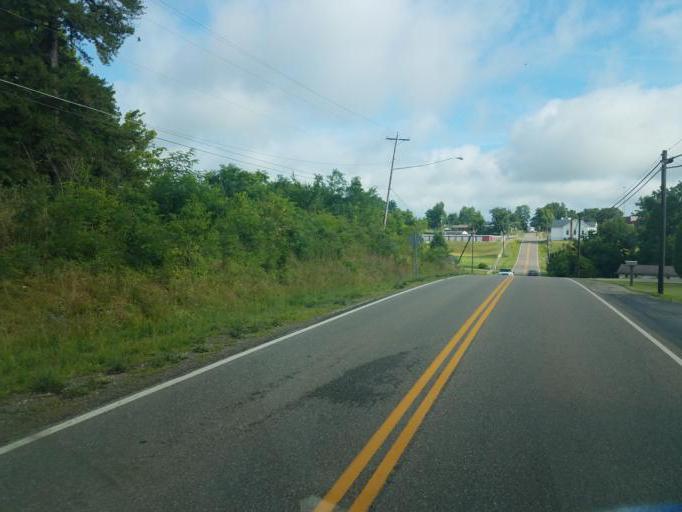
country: US
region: Ohio
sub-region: Gallia County
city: Gallipolis
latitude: 38.8771
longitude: -82.3799
